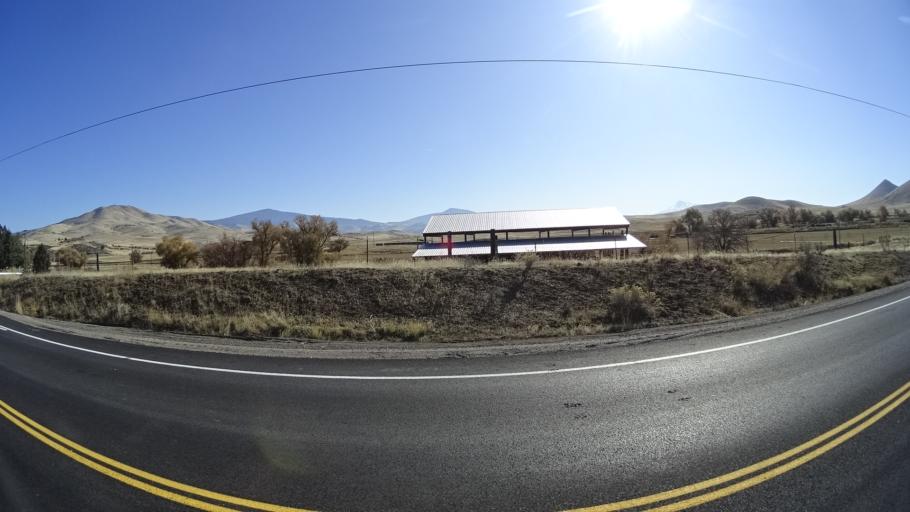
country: US
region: California
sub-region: Siskiyou County
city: Montague
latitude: 41.8481
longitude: -122.4697
